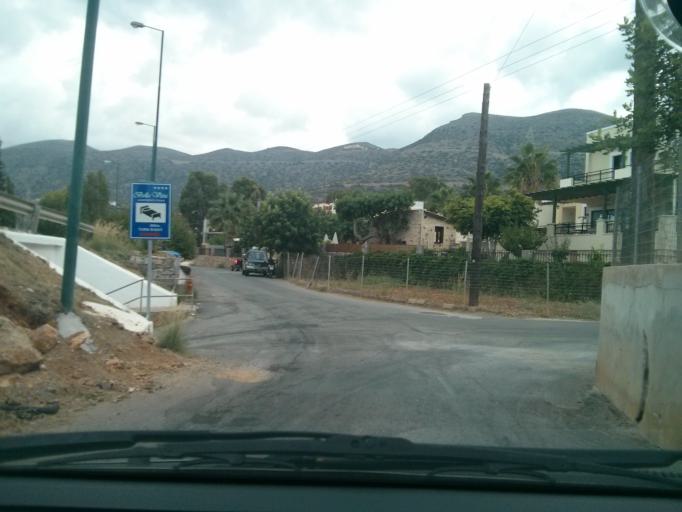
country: GR
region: Crete
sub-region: Nomos Irakleiou
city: Stalis
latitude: 35.2975
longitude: 25.4213
